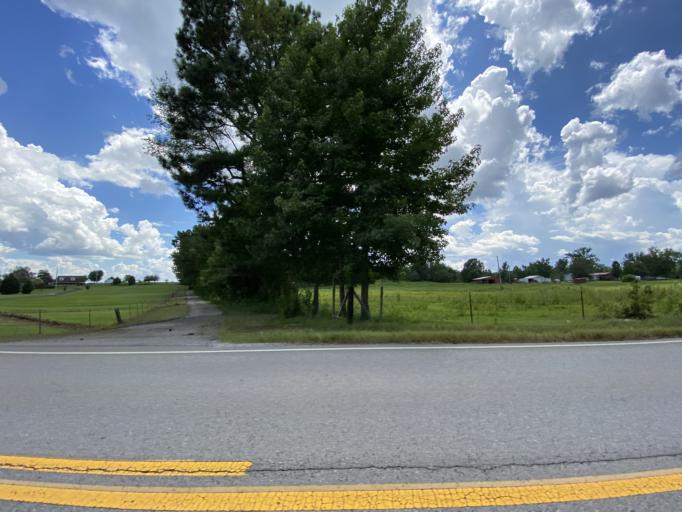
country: US
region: Alabama
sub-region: Lauderdale County
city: Underwood-Petersville
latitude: 34.9471
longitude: -87.8660
